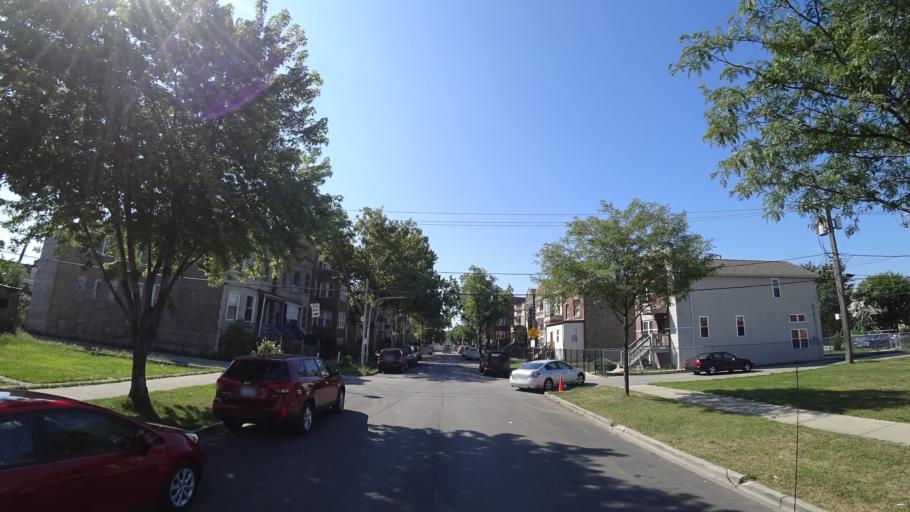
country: US
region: Illinois
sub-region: Cook County
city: Cicero
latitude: 41.8659
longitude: -87.7227
